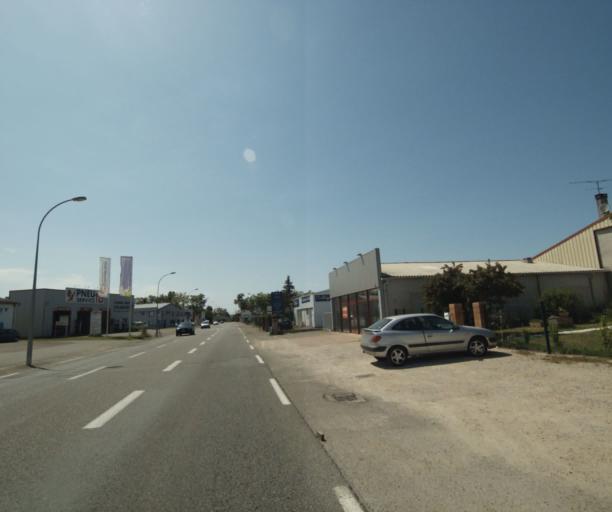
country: FR
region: Midi-Pyrenees
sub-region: Departement du Tarn-et-Garonne
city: Montauban
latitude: 44.0377
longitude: 1.3603
